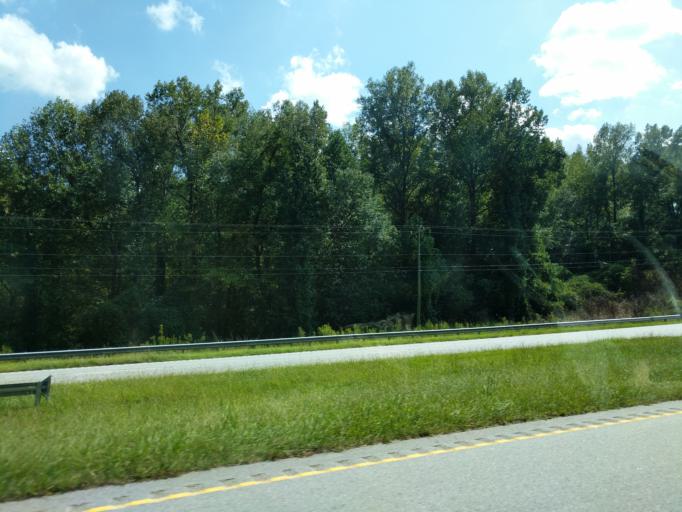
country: US
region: South Carolina
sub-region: Spartanburg County
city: Roebuck
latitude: 34.8124
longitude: -82.0021
